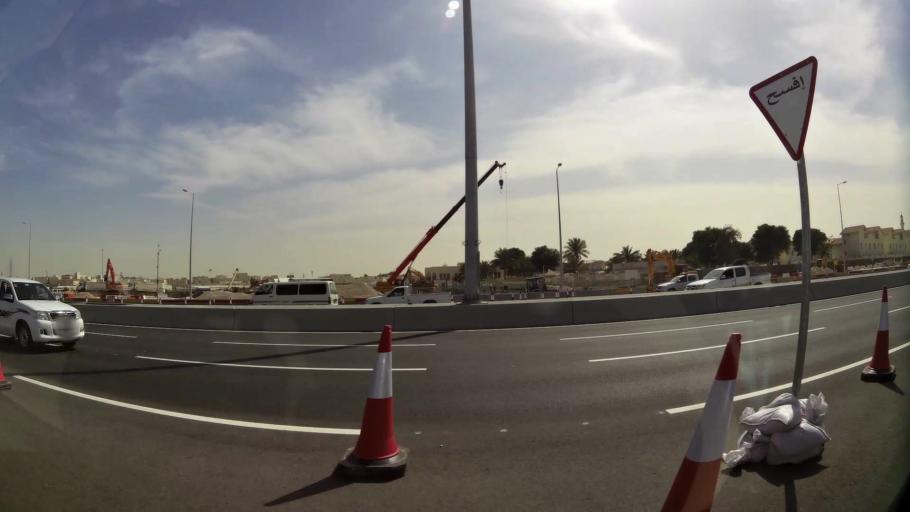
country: QA
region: Baladiyat ar Rayyan
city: Ar Rayyan
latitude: 25.3044
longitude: 51.4179
